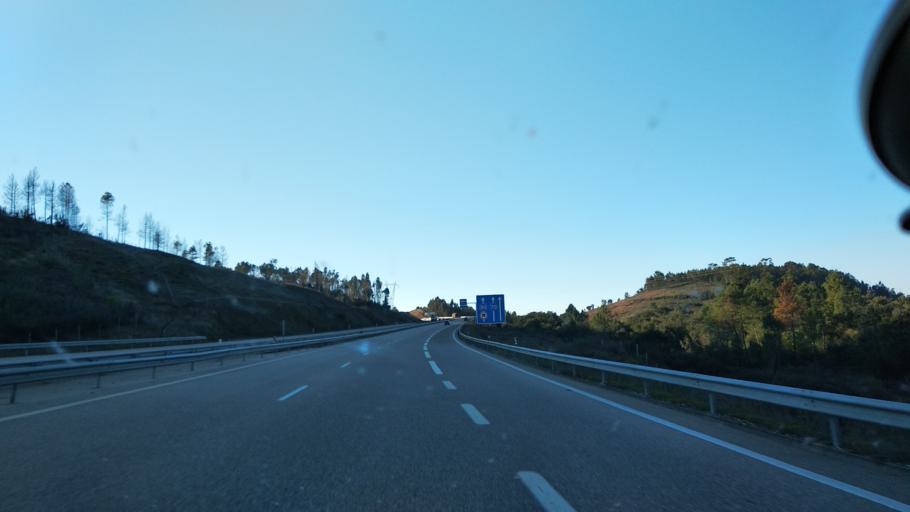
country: PT
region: Santarem
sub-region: Abrantes
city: Alferrarede
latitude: 39.4933
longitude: -8.0696
